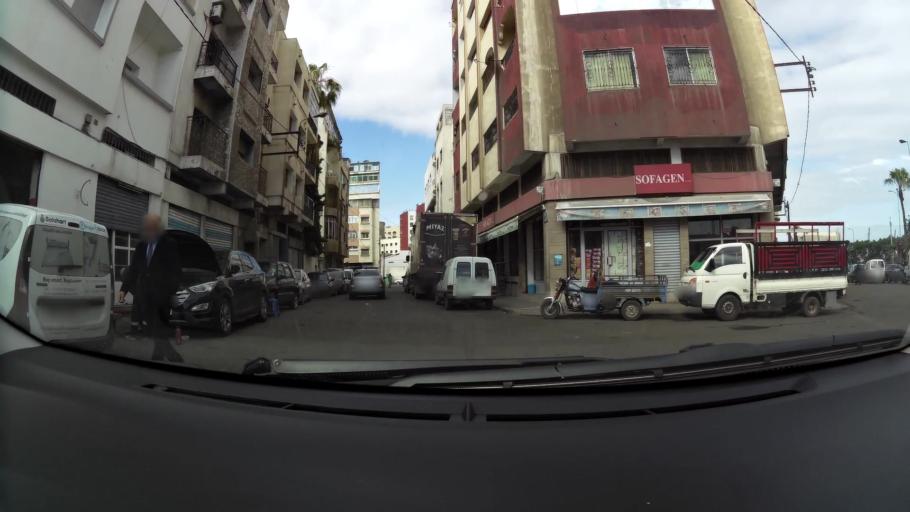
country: MA
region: Grand Casablanca
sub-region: Casablanca
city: Casablanca
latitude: 33.5969
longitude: -7.5906
